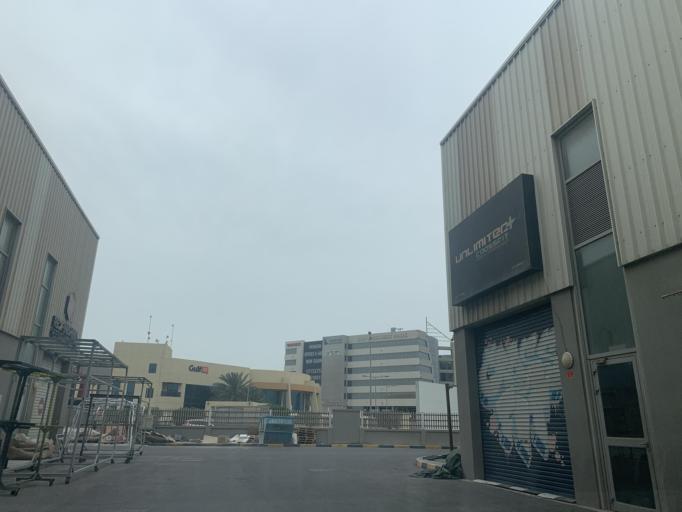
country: BH
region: Muharraq
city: Al Hadd
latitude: 26.2125
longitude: 50.6687
